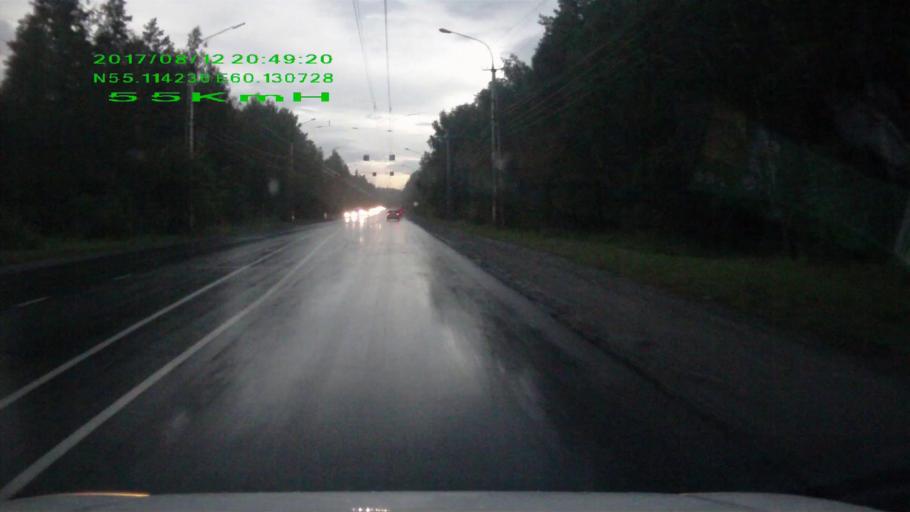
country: RU
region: Chelyabinsk
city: Turgoyak
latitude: 55.1145
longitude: 60.1307
